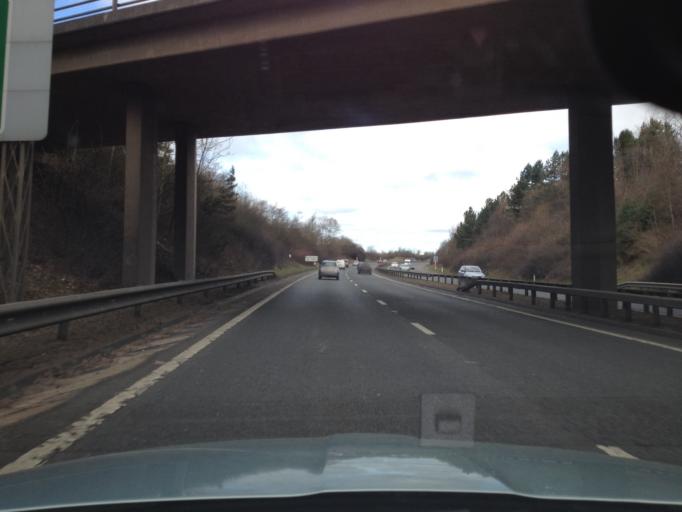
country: GB
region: Scotland
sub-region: Edinburgh
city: Currie
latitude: 55.9135
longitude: -3.2918
